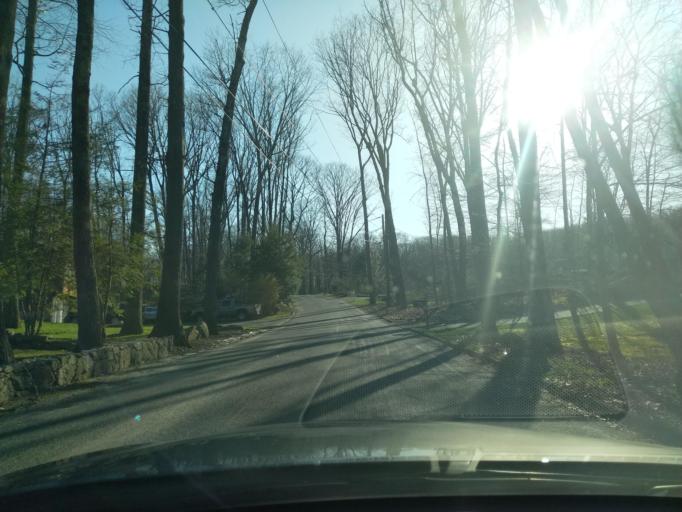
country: US
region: Connecticut
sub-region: Fairfield County
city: Newtown
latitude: 41.3843
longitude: -73.2894
